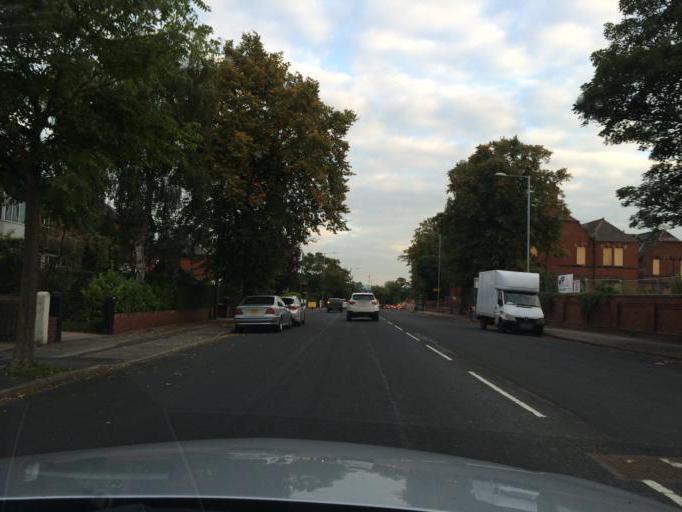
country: GB
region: England
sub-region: Borough of Stockport
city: Hazel Grove
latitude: 53.3934
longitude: -2.1318
